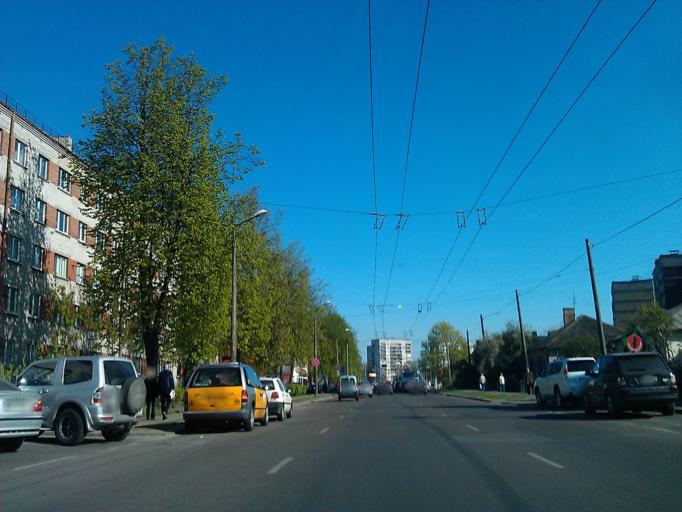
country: LV
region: Riga
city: Riga
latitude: 56.9622
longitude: 24.1718
